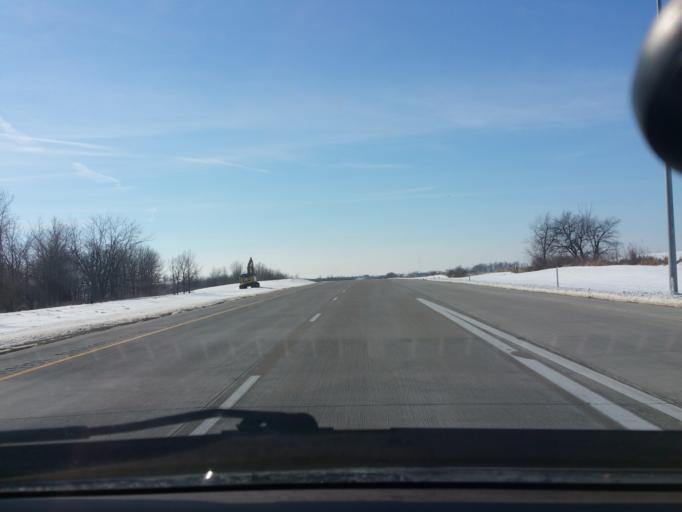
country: US
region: Iowa
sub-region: Decatur County
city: Lamoni
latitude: 40.6194
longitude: -93.8948
